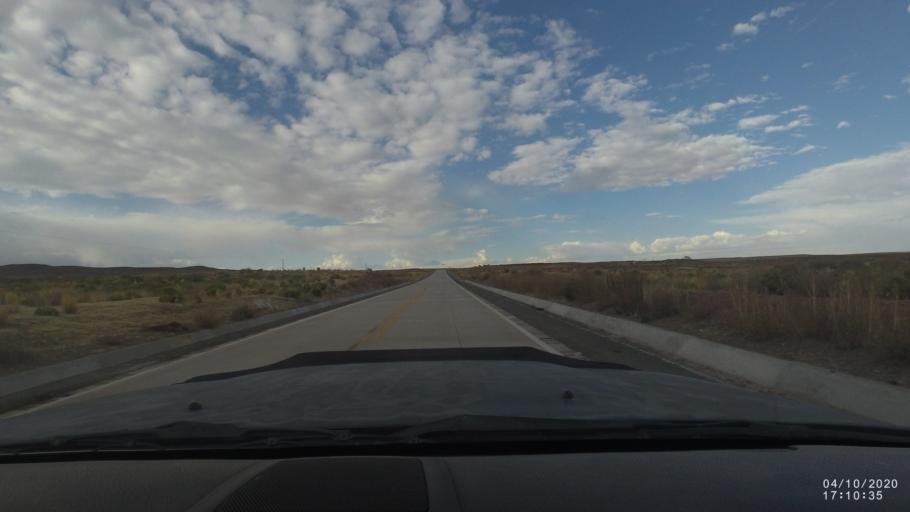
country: BO
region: Oruro
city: Oruro
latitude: -18.3295
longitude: -67.5828
